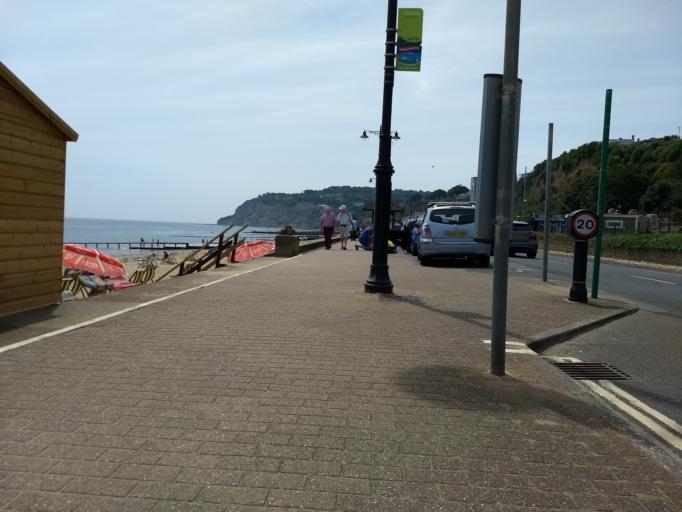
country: GB
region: England
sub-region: Isle of Wight
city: Shanklin
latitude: 50.6332
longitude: -1.1699
